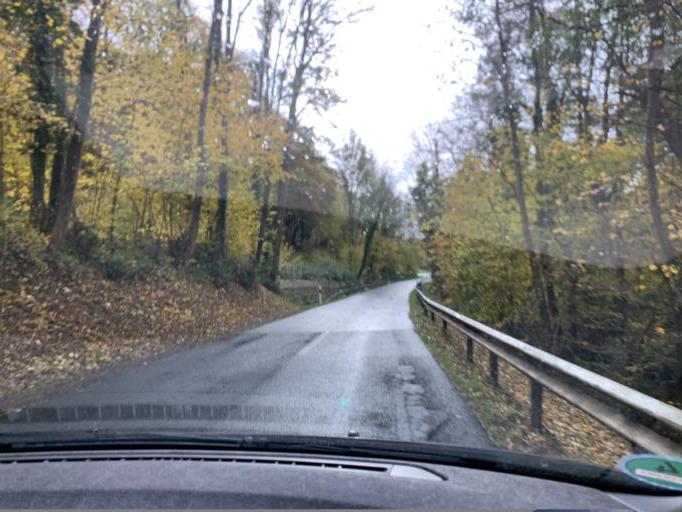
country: DE
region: North Rhine-Westphalia
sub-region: Regierungsbezirk Koln
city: Kreuzau
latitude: 50.7327
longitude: 6.4893
